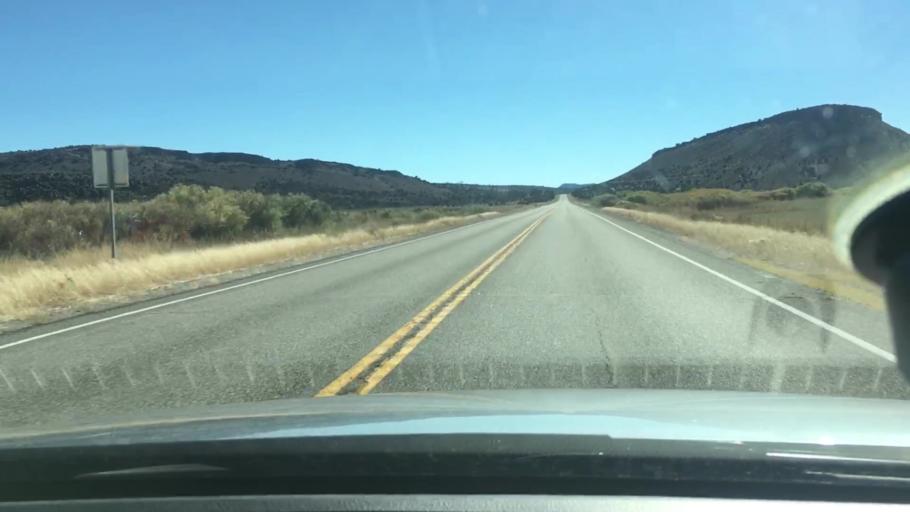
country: US
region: Nevada
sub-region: White Pine County
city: Ely
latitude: 38.9292
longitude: -115.1740
